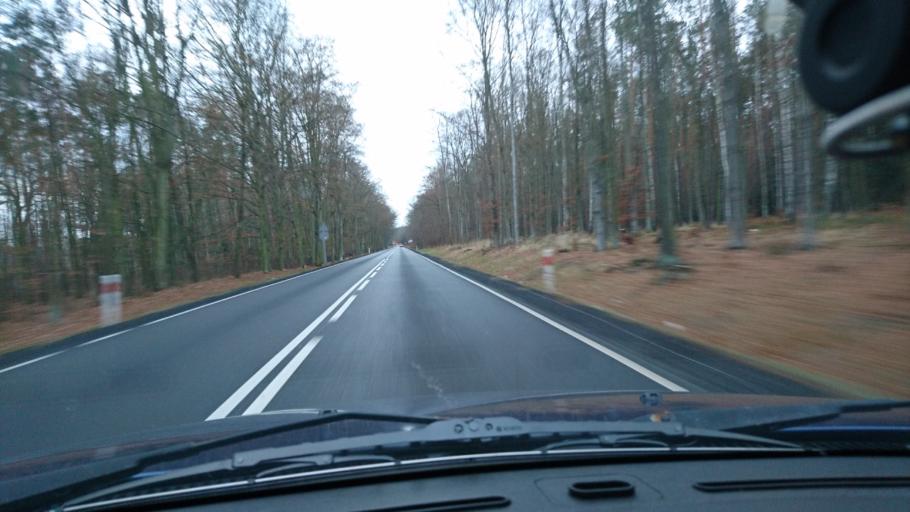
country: PL
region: Opole Voivodeship
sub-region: Powiat kluczborski
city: Kluczbork
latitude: 50.9622
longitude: 18.2866
